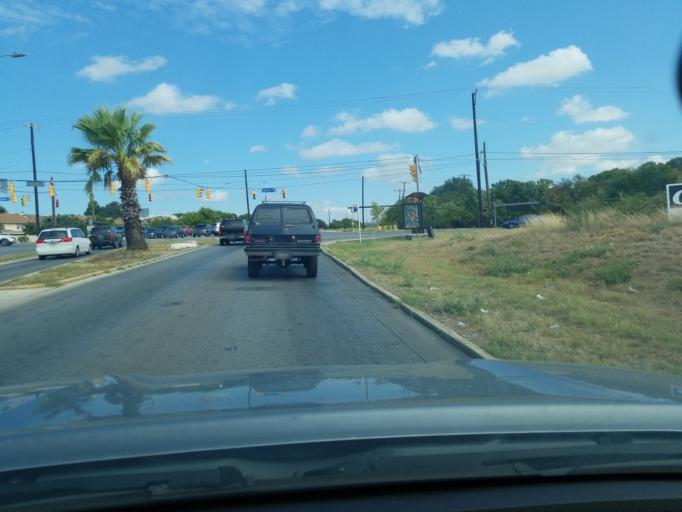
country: US
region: Texas
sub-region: Bexar County
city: Terrell Hills
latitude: 29.4953
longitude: -98.4341
